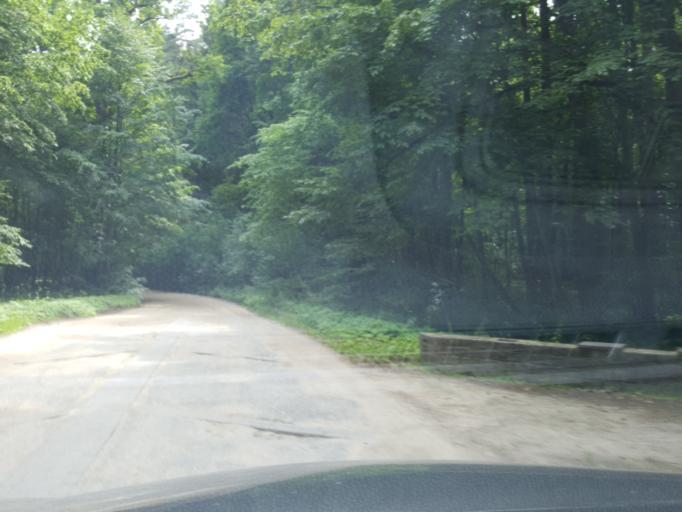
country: LT
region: Alytaus apskritis
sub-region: Alytus
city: Alytus
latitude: 54.3781
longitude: 24.0423
